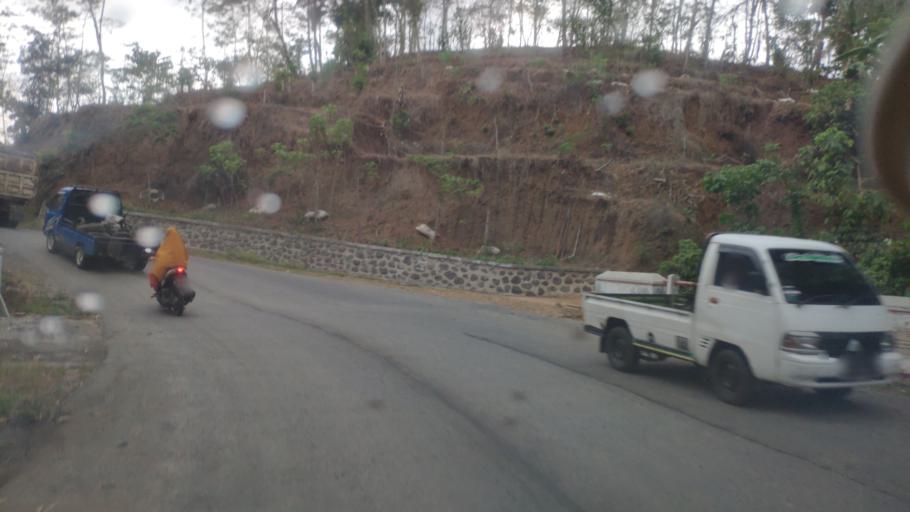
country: ID
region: Central Java
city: Gombong
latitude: -7.4208
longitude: 109.5941
